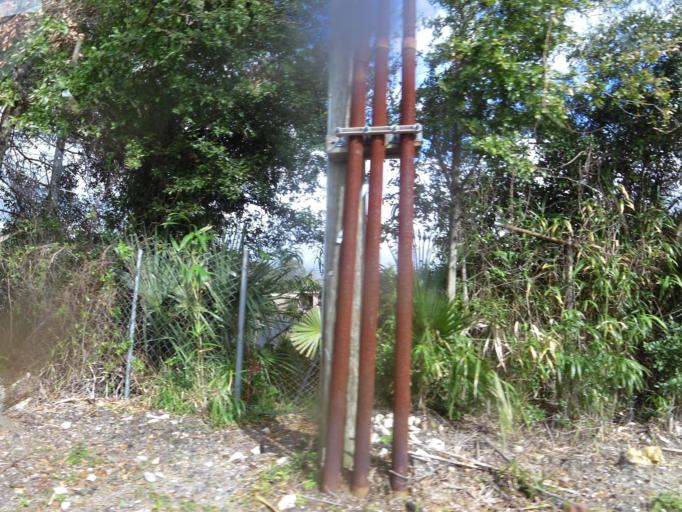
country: US
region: Florida
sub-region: Duval County
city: Jacksonville
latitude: 30.3289
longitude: -81.6015
